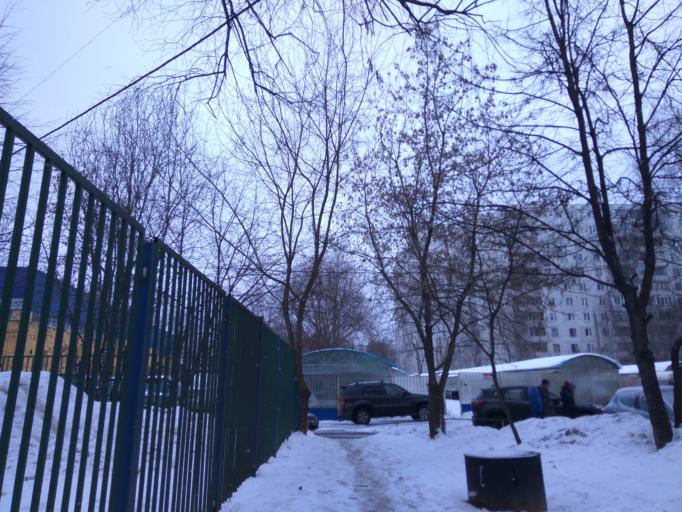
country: RU
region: Moscow
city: Strogino
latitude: 55.7966
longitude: 37.4015
